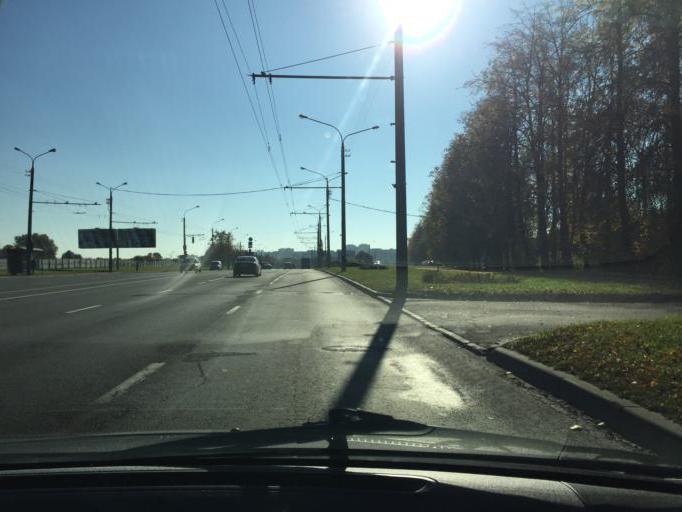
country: BY
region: Minsk
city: Syenitsa
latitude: 53.8632
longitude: 27.5328
